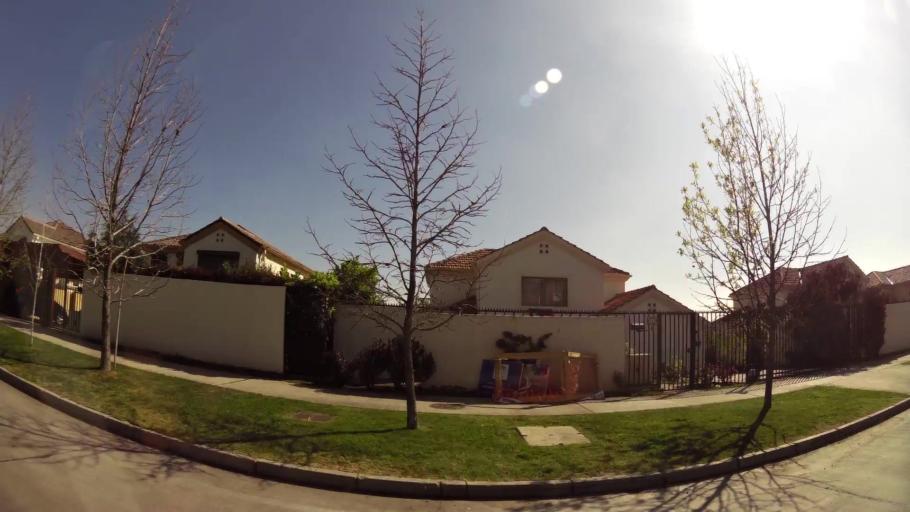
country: CL
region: Santiago Metropolitan
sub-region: Provincia de Santiago
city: Villa Presidente Frei, Nunoa, Santiago, Chile
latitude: -33.4080
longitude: -70.5071
